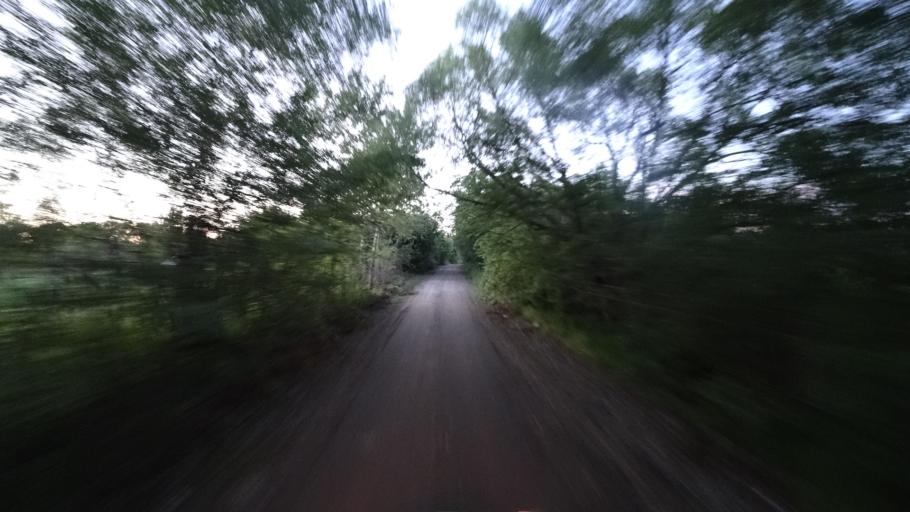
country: RU
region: Khabarovsk Krai
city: Khor
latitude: 47.8562
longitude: 134.9414
